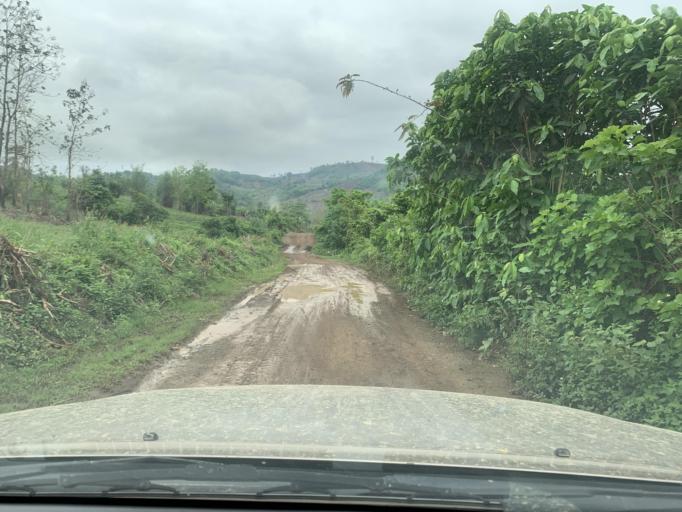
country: TH
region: Uttaradit
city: Ban Khok
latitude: 18.3964
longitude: 101.4297
